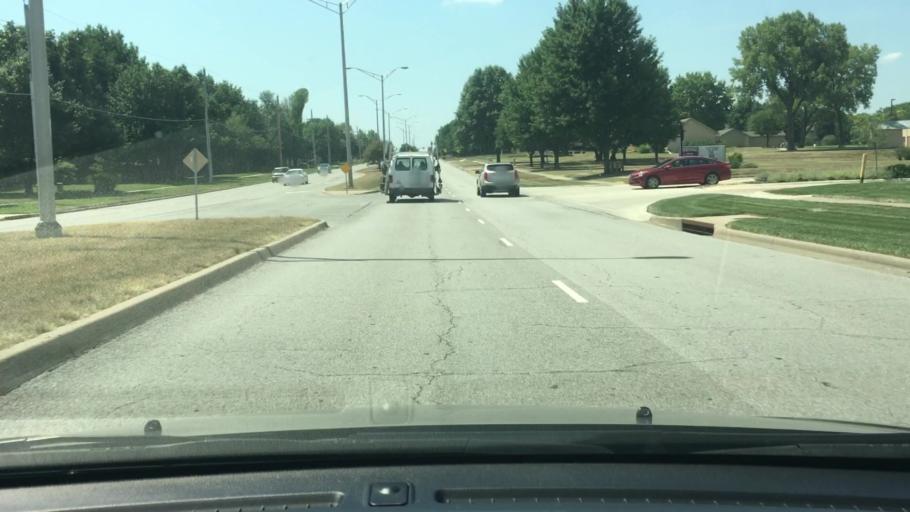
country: US
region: Kansas
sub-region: Johnson County
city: Lenexa
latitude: 38.8956
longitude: -94.7238
